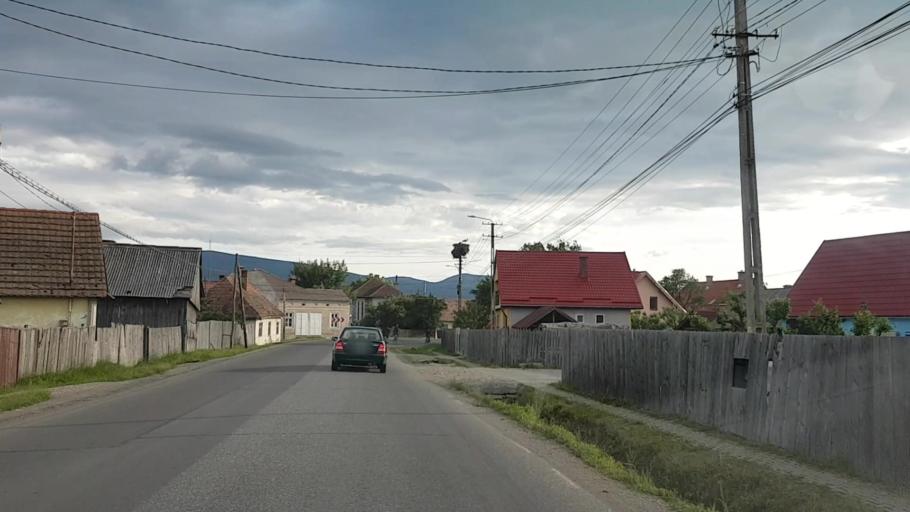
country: RO
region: Harghita
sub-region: Comuna Joseni
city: Joseni
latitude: 46.7032
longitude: 25.5148
